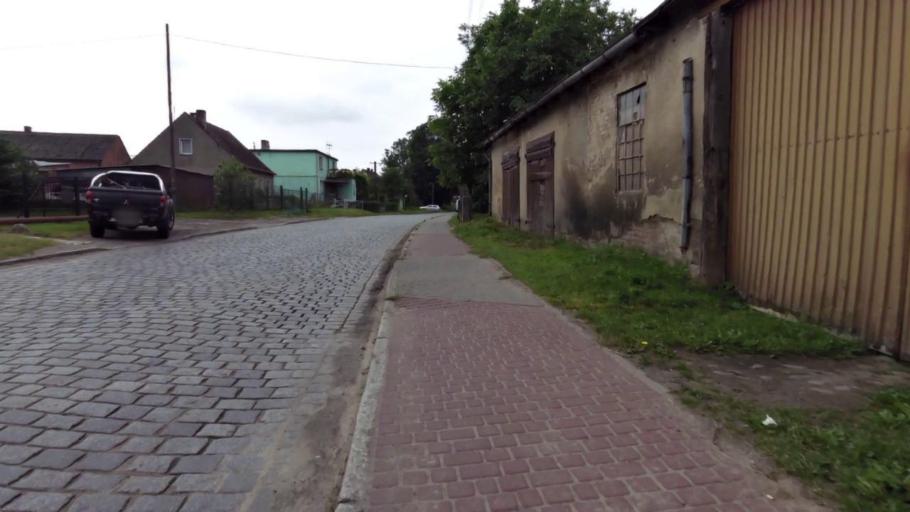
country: PL
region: West Pomeranian Voivodeship
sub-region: Powiat kamienski
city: Wolin
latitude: 53.8425
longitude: 14.6276
